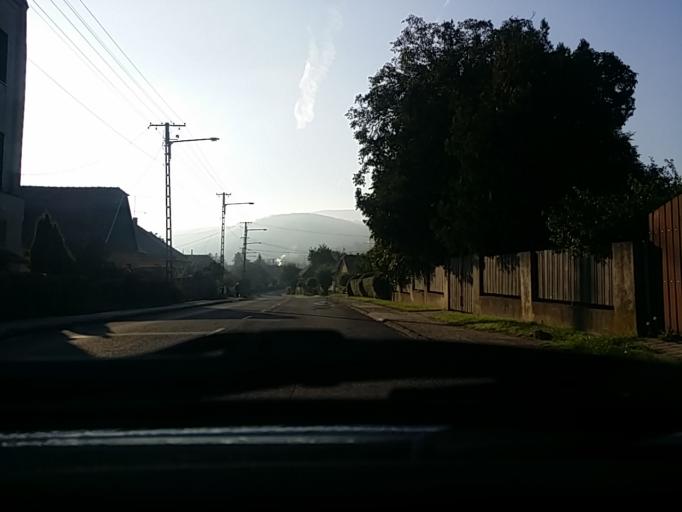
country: HU
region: Komarom-Esztergom
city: Pilismarot
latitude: 47.7675
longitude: 18.9040
